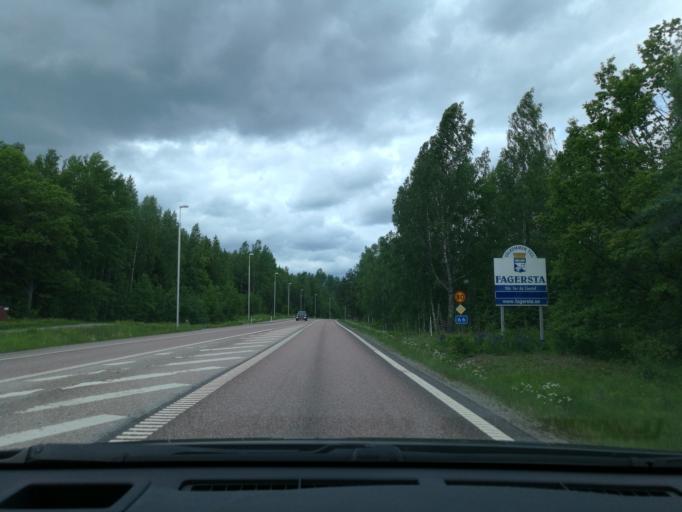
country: SE
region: Vaestmanland
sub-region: Fagersta Kommun
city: Fagersta
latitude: 59.9784
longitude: 15.8205
